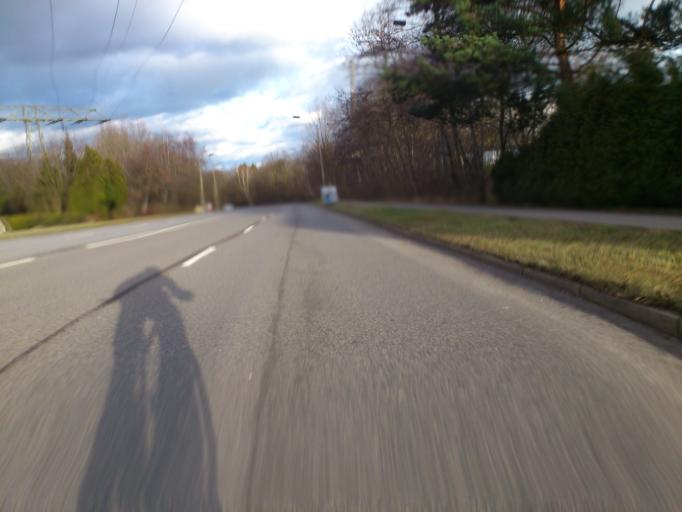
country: DE
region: Saxony
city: Neukirchen
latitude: 50.7926
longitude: 12.9062
